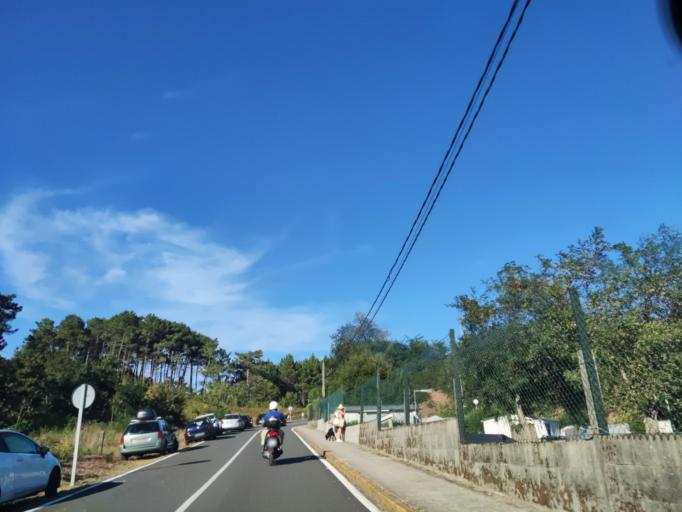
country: ES
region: Galicia
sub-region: Provincia da Coruna
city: Boiro
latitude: 42.5881
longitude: -8.9258
